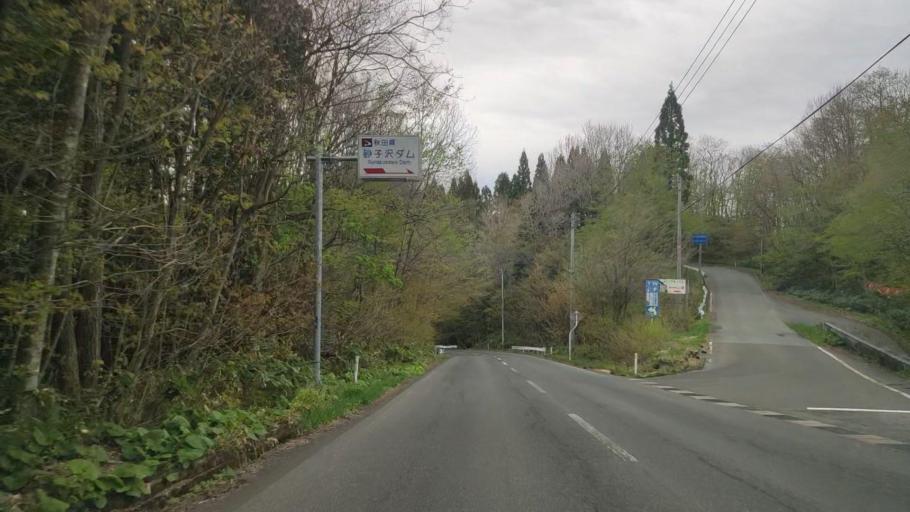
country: JP
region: Akita
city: Hanawa
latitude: 40.3704
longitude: 140.7837
